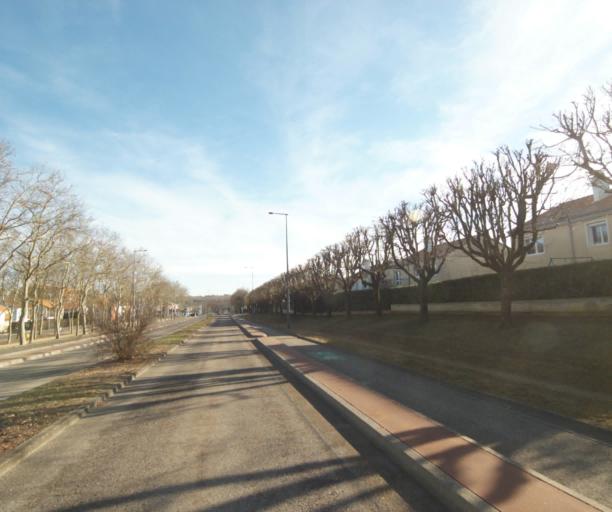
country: FR
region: Lorraine
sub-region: Departement de Meurthe-et-Moselle
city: Chavigny
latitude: 48.6563
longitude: 6.1101
